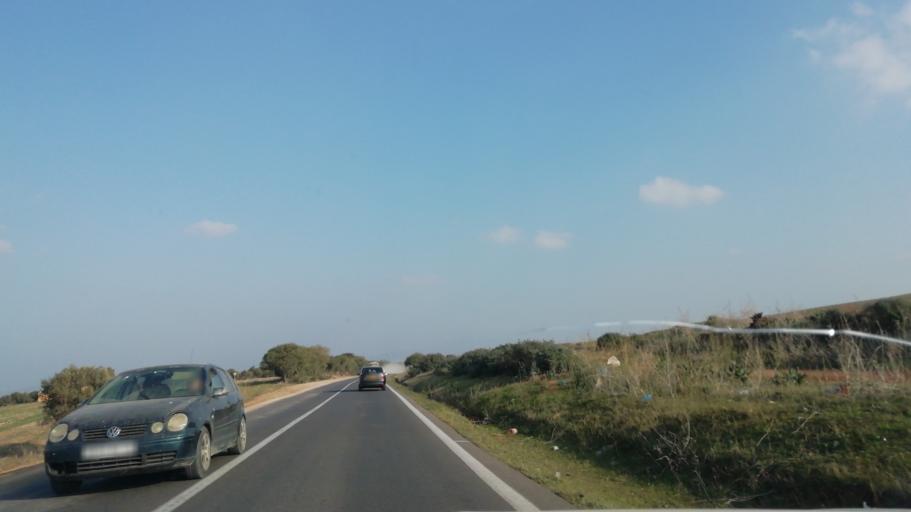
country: DZ
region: Ain Temouchent
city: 'Ain Temouchent
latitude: 35.3052
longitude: -1.0549
